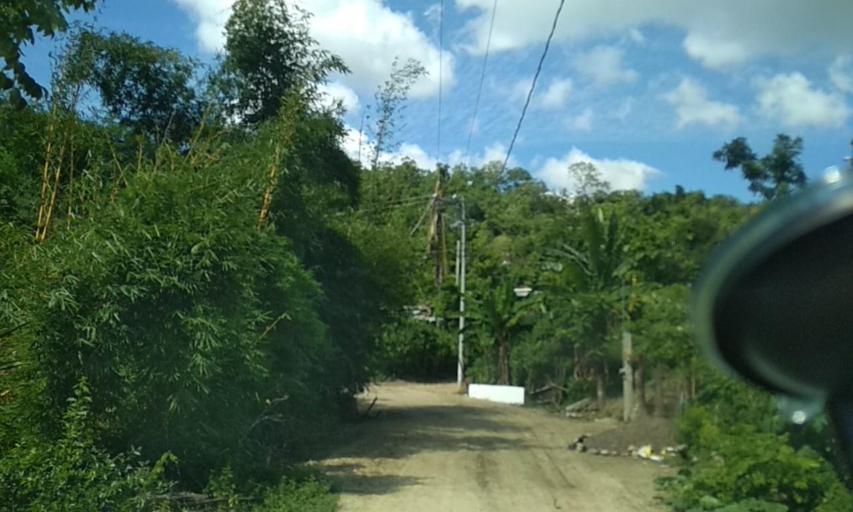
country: MX
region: Veracruz
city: Cazones de Herrera
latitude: 20.6235
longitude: -97.3253
